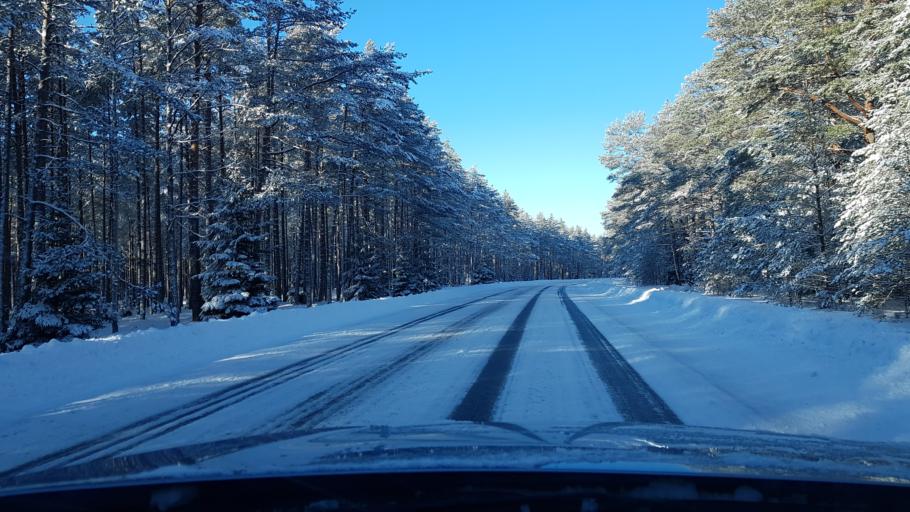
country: EE
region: Hiiumaa
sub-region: Kaerdla linn
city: Kardla
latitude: 58.9265
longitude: 22.7873
